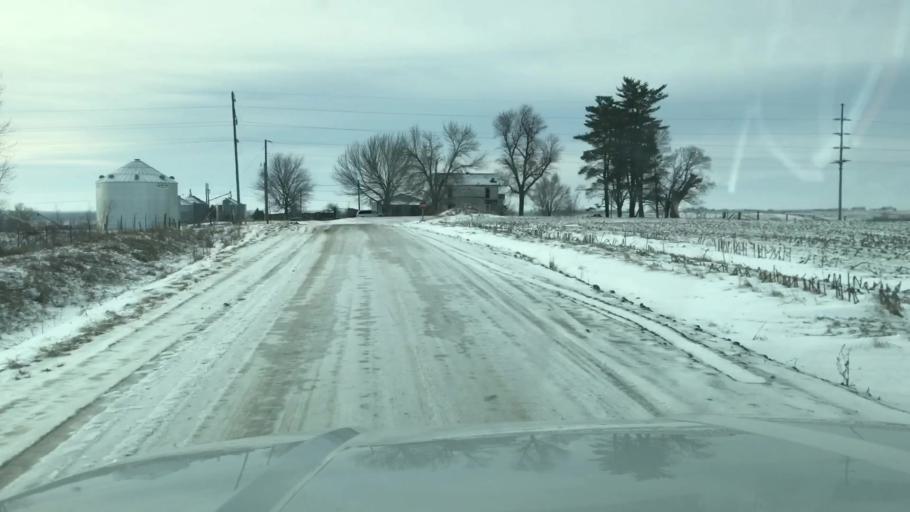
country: US
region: Missouri
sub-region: Holt County
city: Mound City
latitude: 40.1309
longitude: -95.0697
